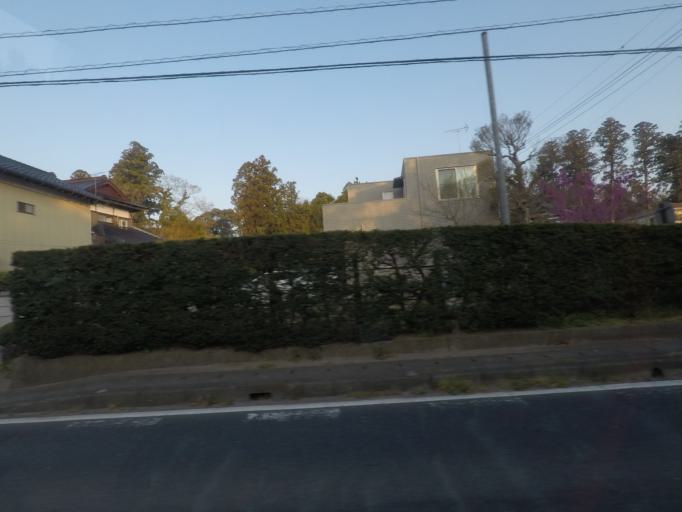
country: JP
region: Chiba
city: Narita
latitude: 35.8254
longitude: 140.4106
